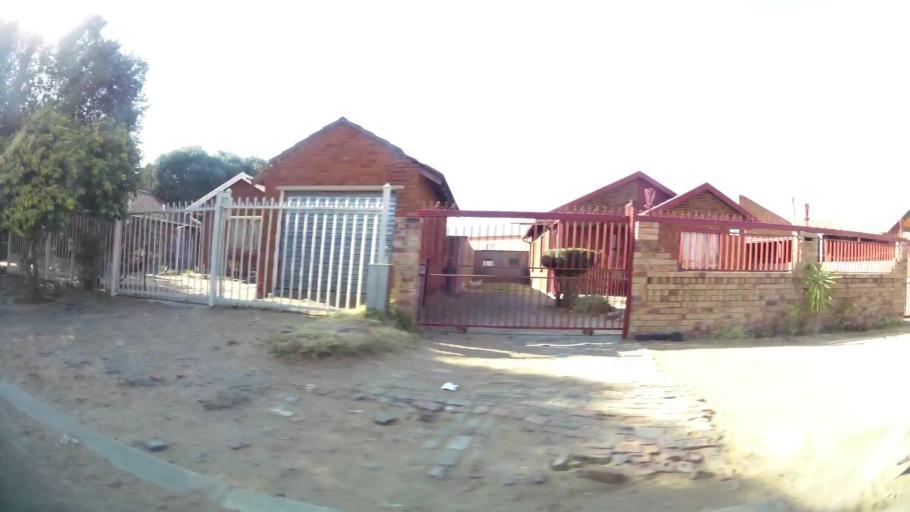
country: ZA
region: Orange Free State
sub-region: Mangaung Metropolitan Municipality
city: Bloemfontein
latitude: -29.1825
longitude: 26.2235
